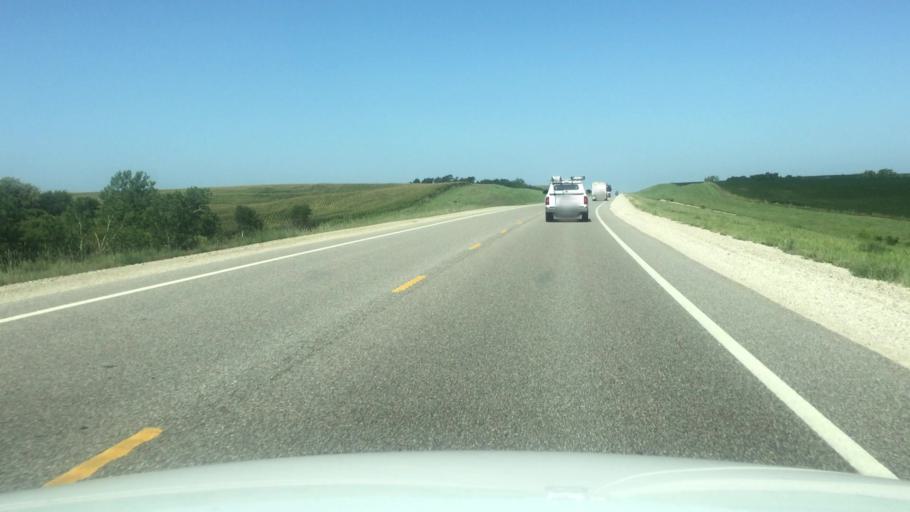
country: US
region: Kansas
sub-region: Doniphan County
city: Troy
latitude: 39.7985
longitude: -95.1613
